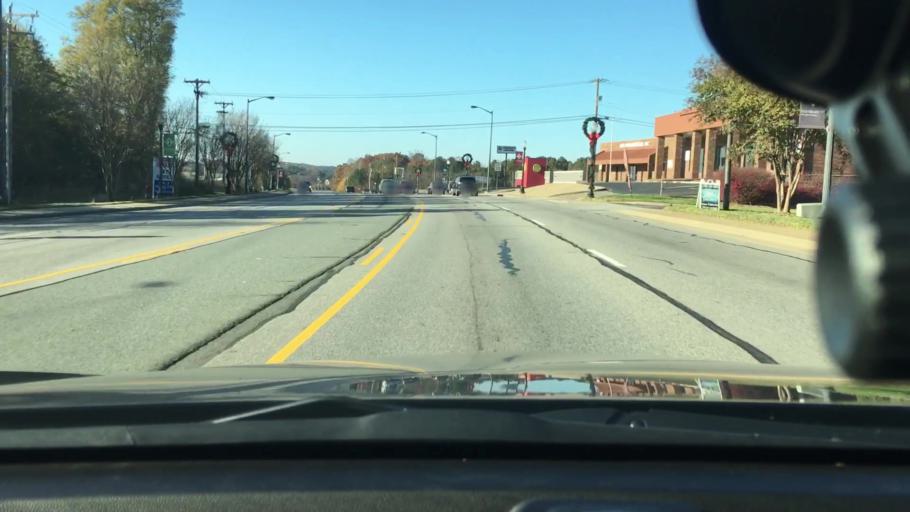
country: US
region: North Carolina
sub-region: Cabarrus County
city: Harrisburg
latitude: 35.3199
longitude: -80.6710
